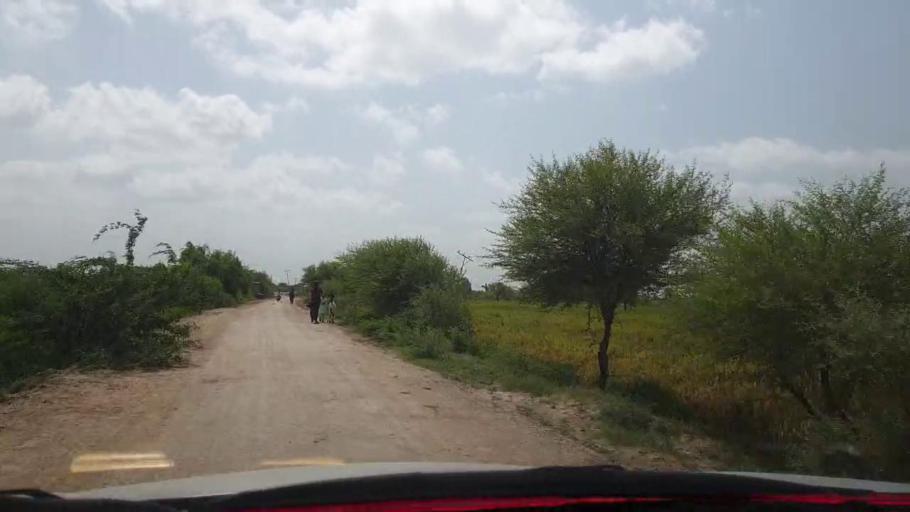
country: PK
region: Sindh
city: Talhar
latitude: 24.9056
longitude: 68.8469
